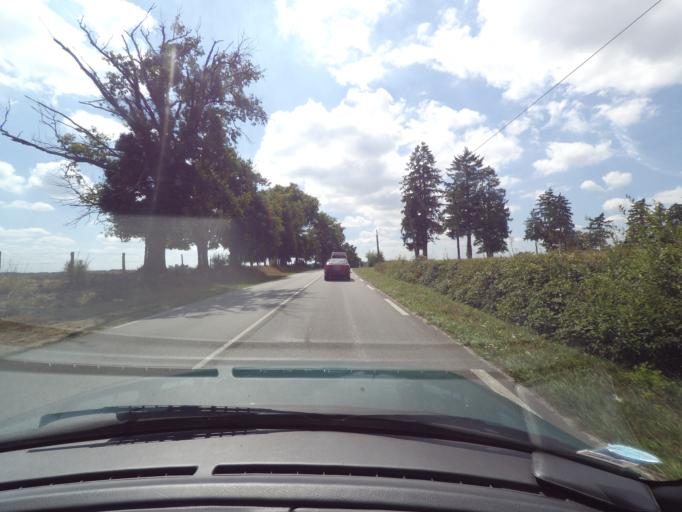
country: FR
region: Limousin
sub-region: Departement de la Haute-Vienne
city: Limoges
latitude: 45.7989
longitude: 1.2523
